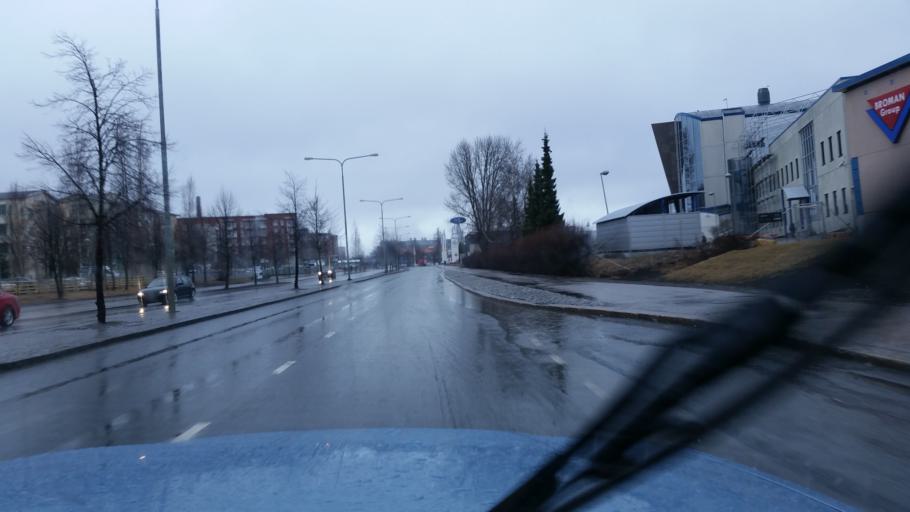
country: FI
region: Pirkanmaa
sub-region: Tampere
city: Tampere
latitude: 61.4795
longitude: 23.7635
